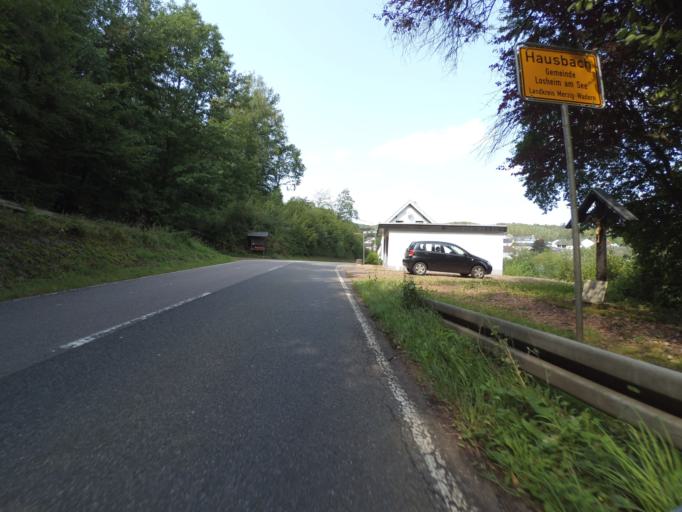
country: DE
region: Saarland
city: Britten
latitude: 49.5054
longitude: 6.6886
